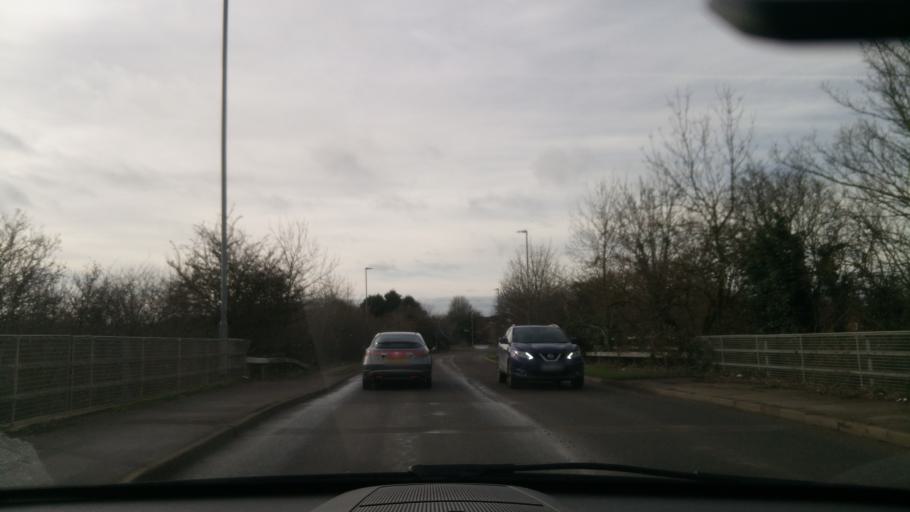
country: GB
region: England
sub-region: Peterborough
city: Eye
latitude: 52.6031
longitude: -0.2265
